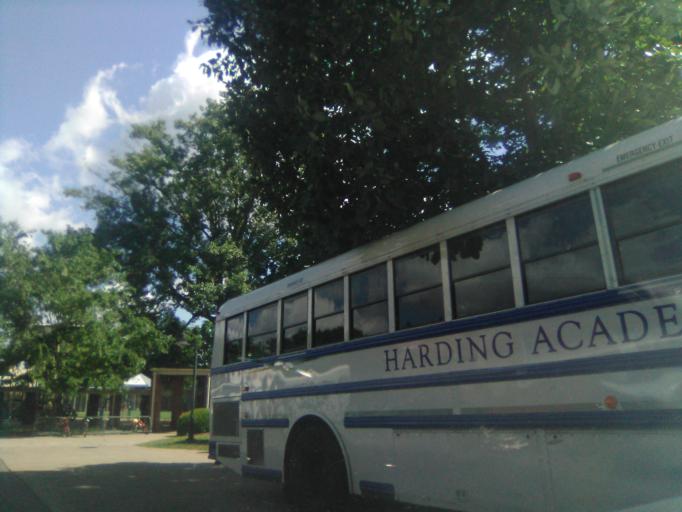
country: US
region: Tennessee
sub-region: Davidson County
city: Belle Meade
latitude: 36.1020
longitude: -86.8669
